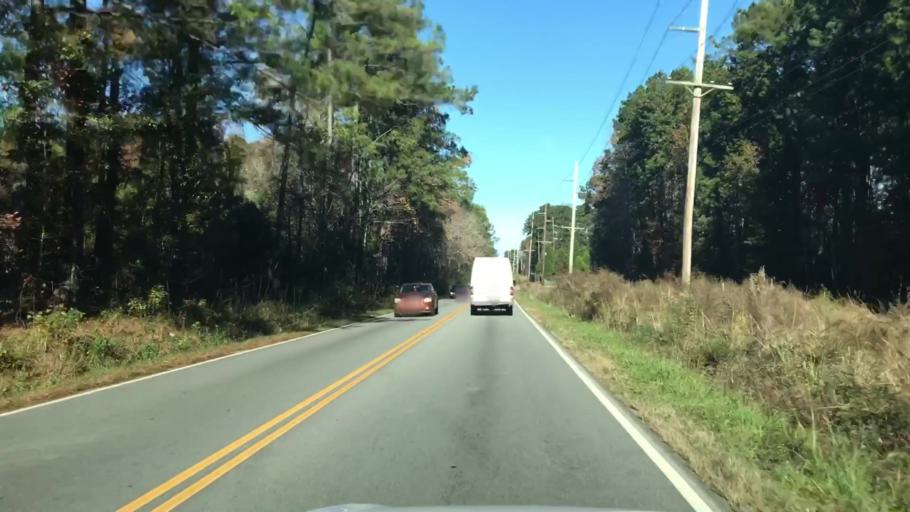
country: US
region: South Carolina
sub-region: Dorchester County
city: Centerville
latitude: 32.9841
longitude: -80.2192
